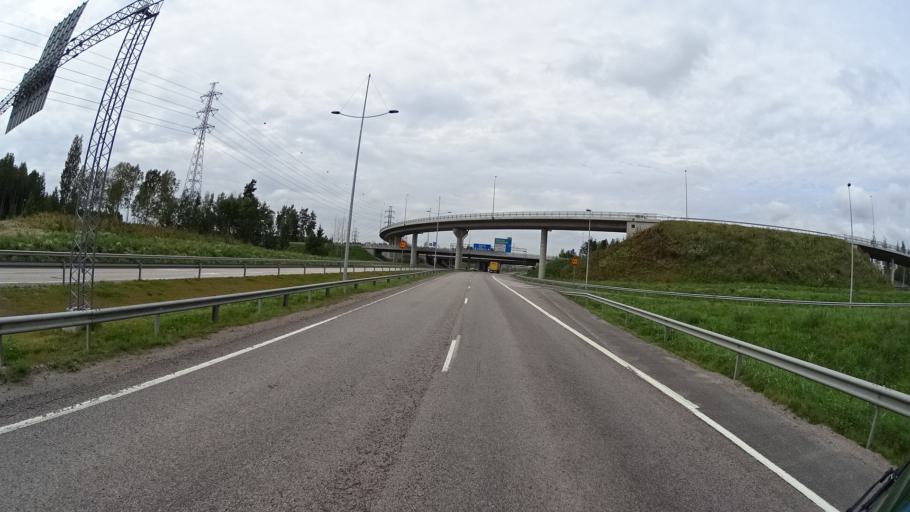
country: FI
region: Uusimaa
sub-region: Helsinki
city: Vantaa
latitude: 60.2561
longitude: 25.1281
